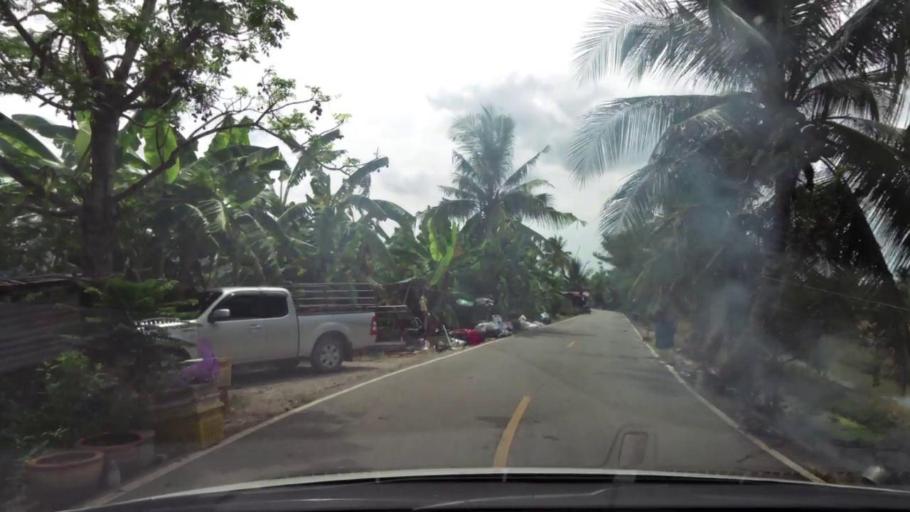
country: TH
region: Ratchaburi
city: Damnoen Saduak
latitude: 13.5109
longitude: 100.0120
